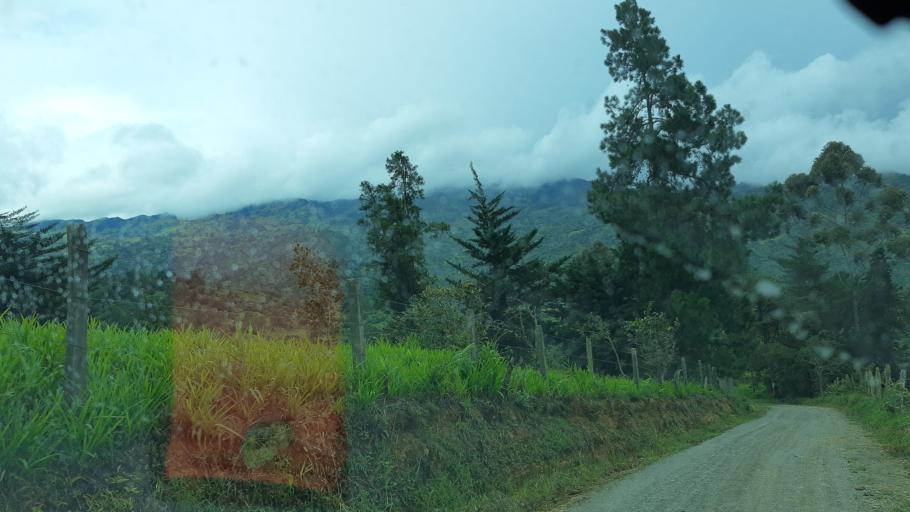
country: CO
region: Boyaca
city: Garagoa
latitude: 5.0379
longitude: -73.3581
